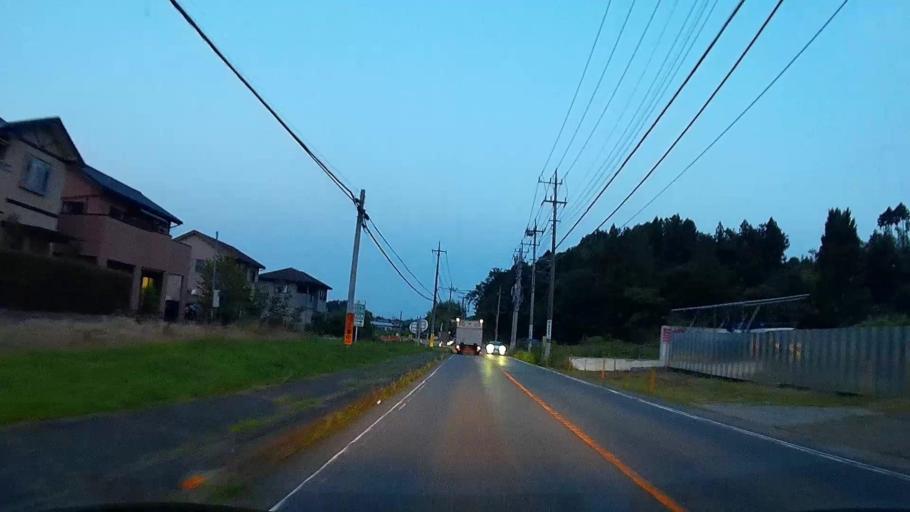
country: JP
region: Gunma
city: Annaka
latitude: 36.3580
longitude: 138.9233
